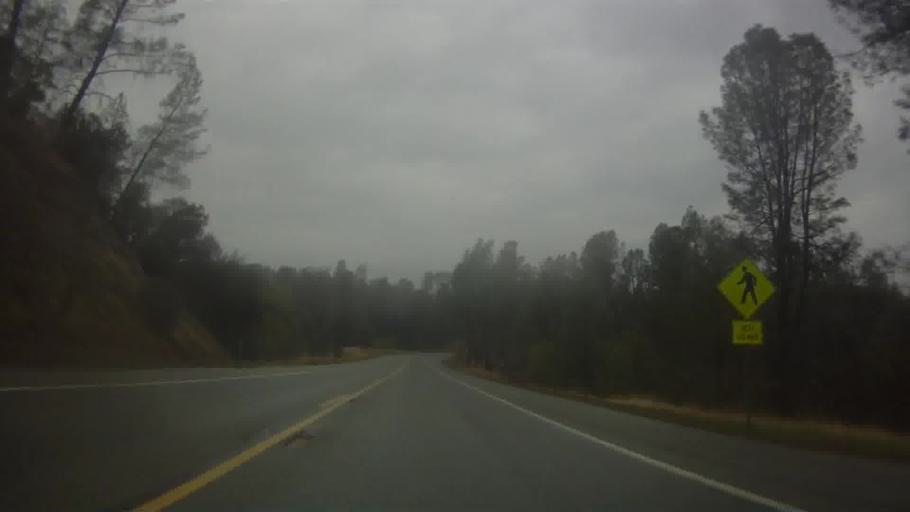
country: US
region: California
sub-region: Shasta County
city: Shasta
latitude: 40.5862
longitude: -122.4532
